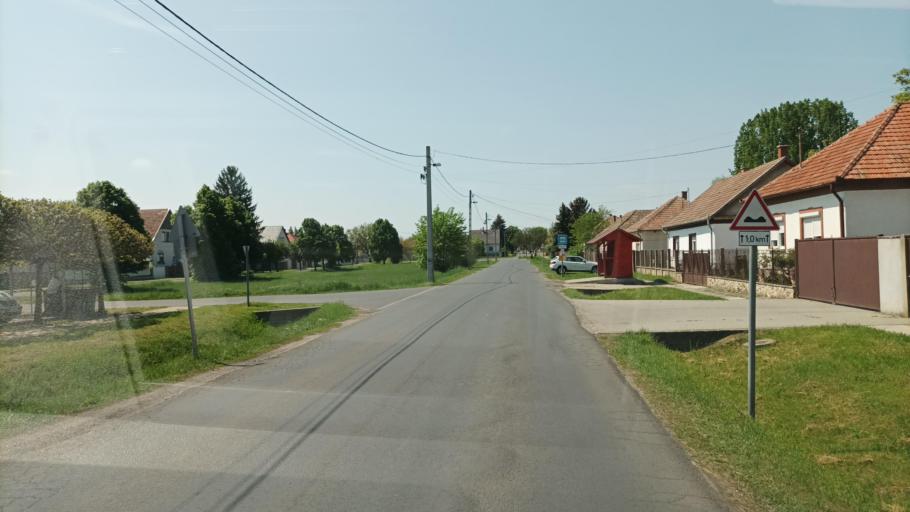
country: HU
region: Pest
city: Szentmartonkata
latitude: 47.4470
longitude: 19.6927
